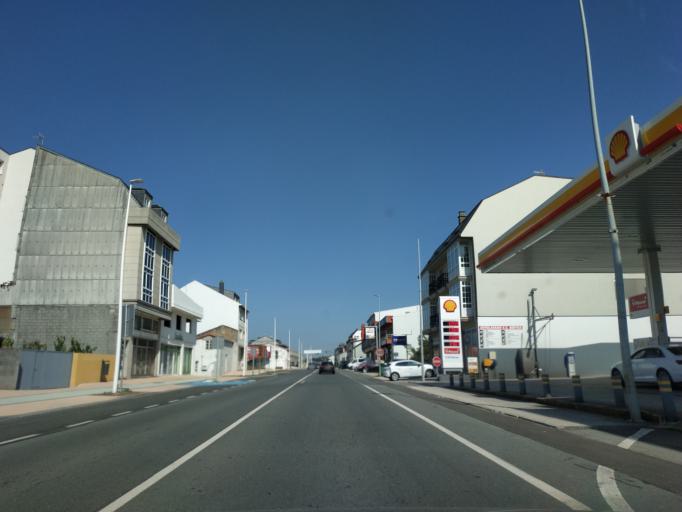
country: ES
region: Galicia
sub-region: Provincia da Coruna
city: Carballo
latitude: 43.2221
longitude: -8.6840
